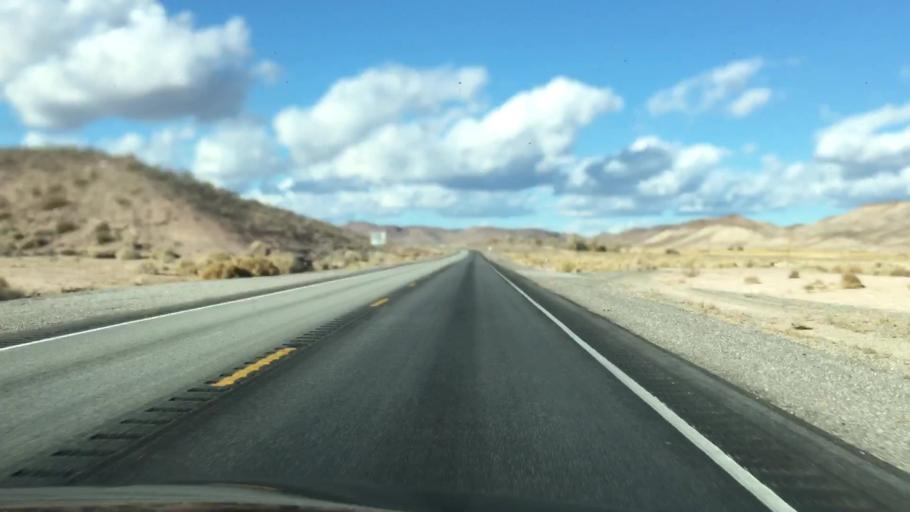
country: US
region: Nevada
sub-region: Nye County
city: Beatty
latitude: 36.9947
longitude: -116.7254
